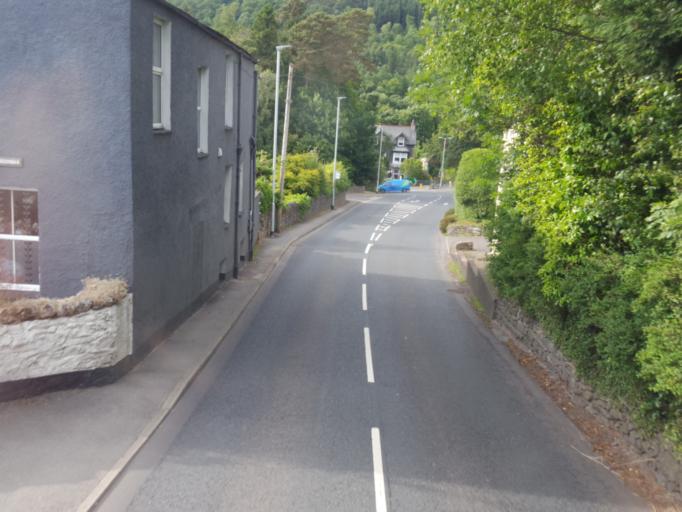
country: GB
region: England
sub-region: Cumbria
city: Keswick
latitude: 54.6026
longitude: -3.1167
